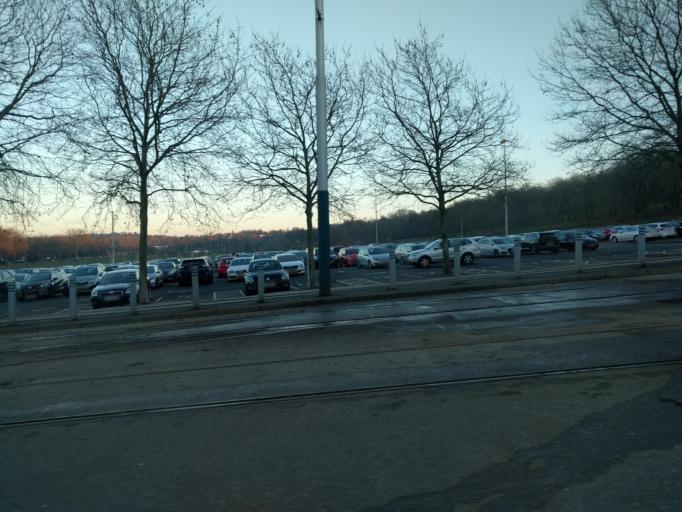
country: GB
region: England
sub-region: Nottingham
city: Nottingham
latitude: 52.9650
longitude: -1.1668
